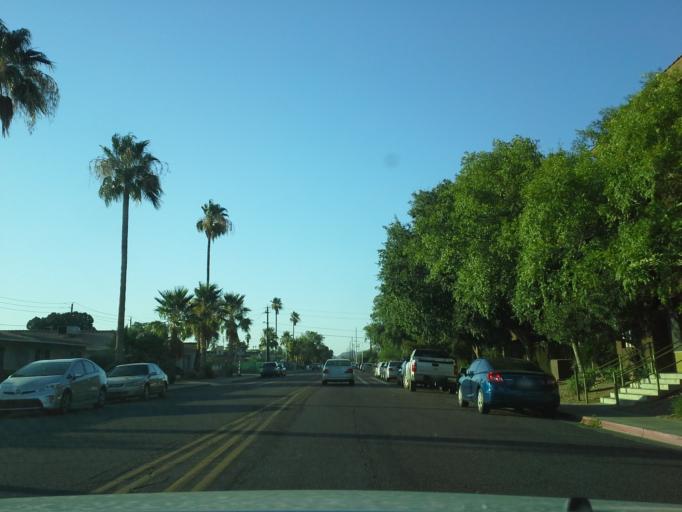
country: US
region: Arizona
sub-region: Maricopa County
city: Phoenix
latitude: 33.4957
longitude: -112.0782
